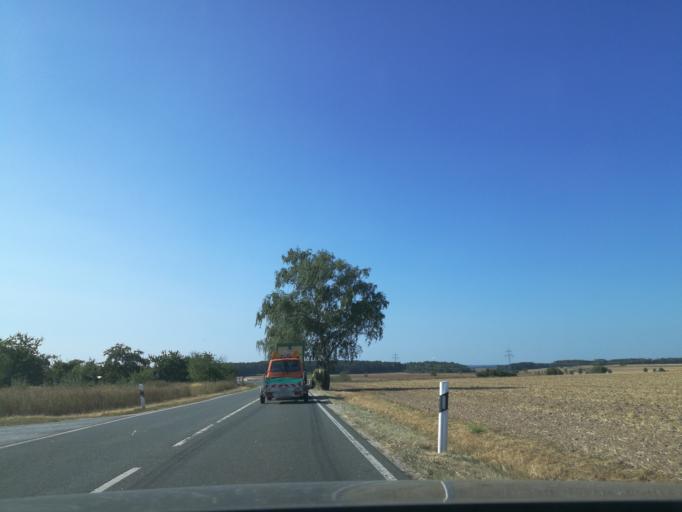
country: DE
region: Bavaria
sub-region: Regierungsbezirk Mittelfranken
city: Cadolzburg
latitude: 49.4481
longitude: 10.8480
